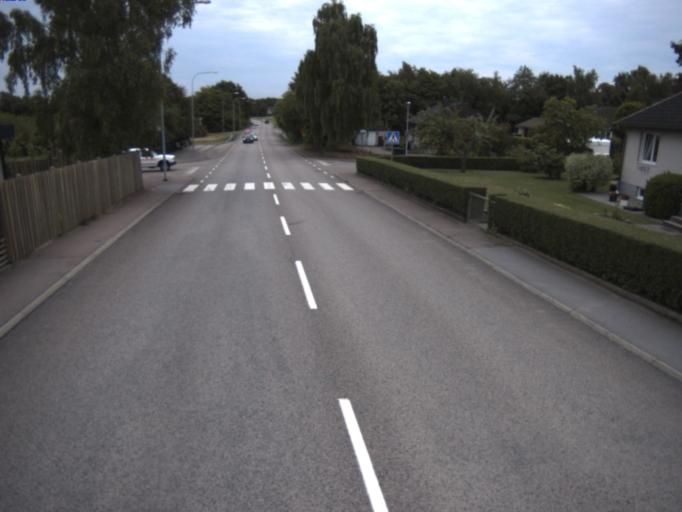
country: SE
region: Skane
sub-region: Helsingborg
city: Odakra
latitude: 56.1029
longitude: 12.7524
